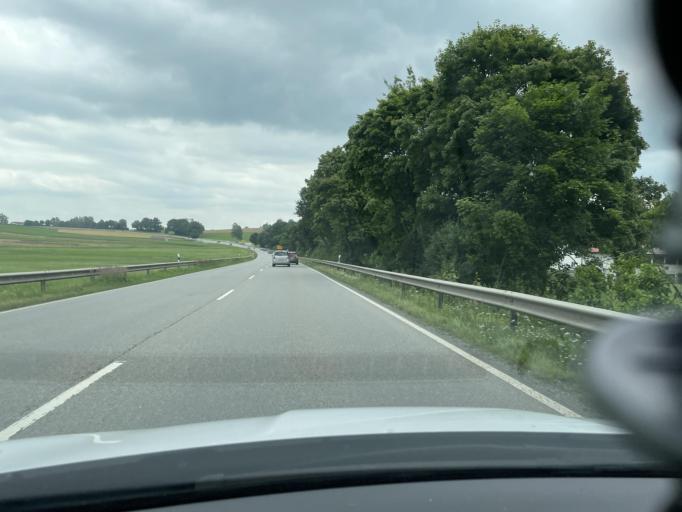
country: DE
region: Bavaria
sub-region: Upper Bavaria
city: Wasserburg am Inn
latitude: 48.0808
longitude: 12.2049
